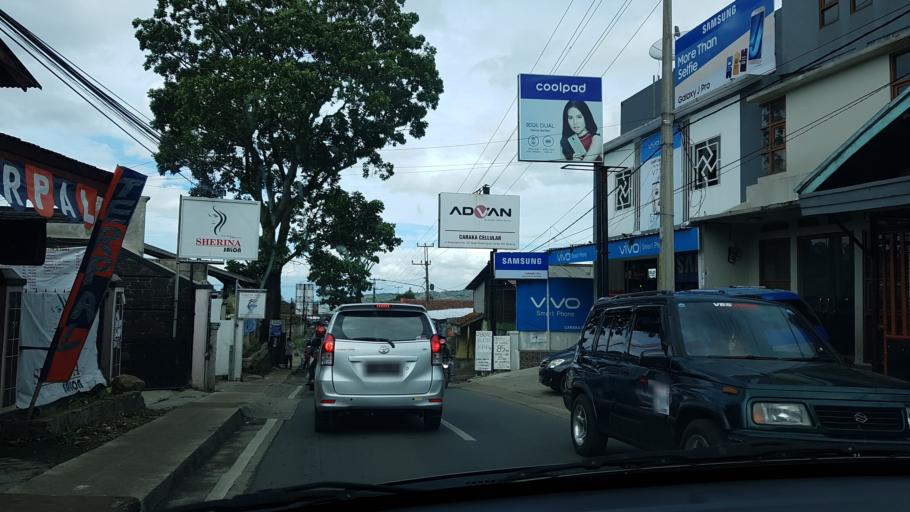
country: ID
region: West Java
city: Banjar
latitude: -7.1059
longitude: 107.4570
